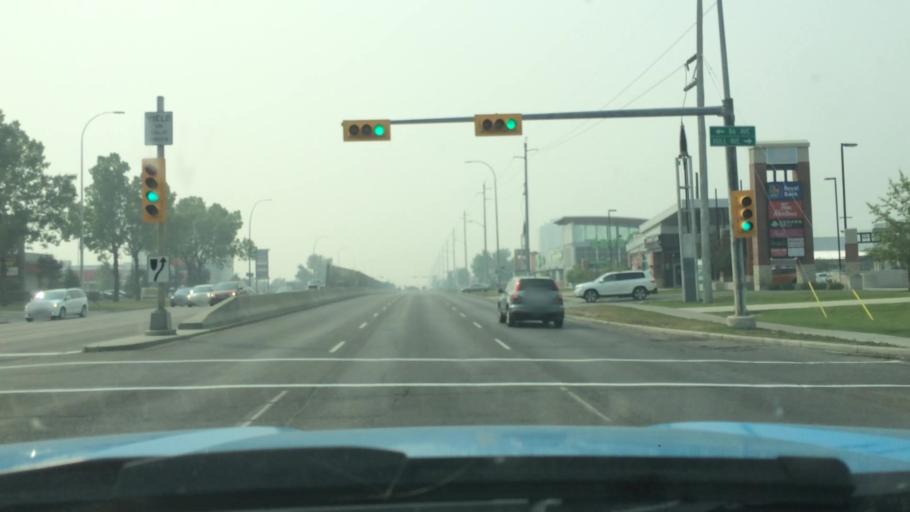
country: CA
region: Alberta
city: Calgary
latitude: 50.9759
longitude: -114.0717
